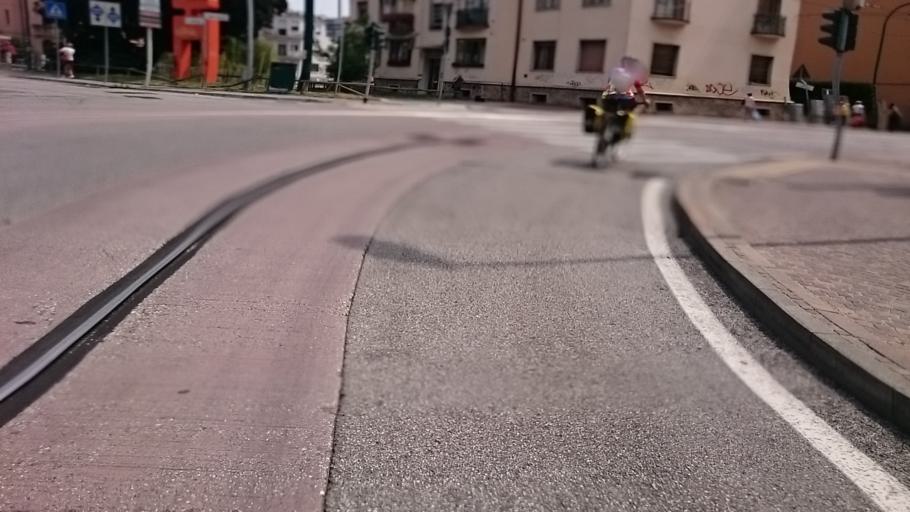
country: IT
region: Veneto
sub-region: Provincia di Venezia
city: Mestre
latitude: 45.4934
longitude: 12.2462
